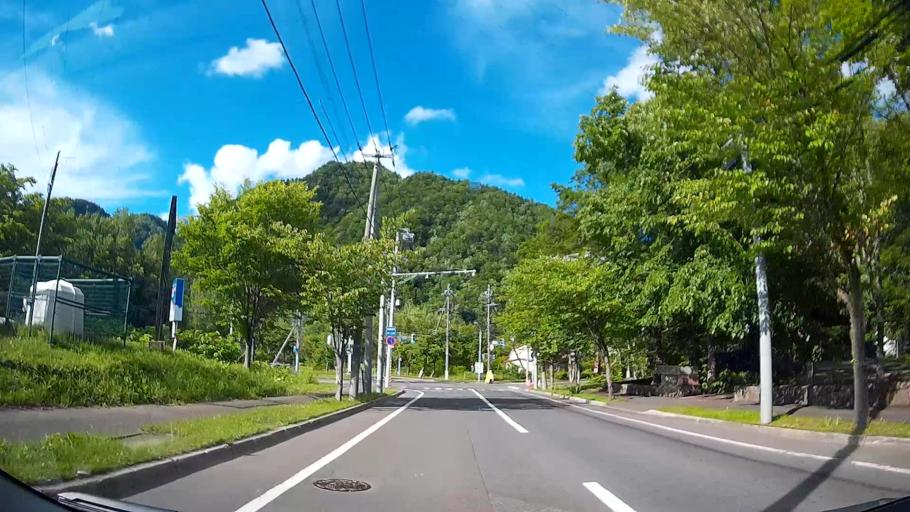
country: JP
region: Hokkaido
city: Sapporo
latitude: 42.9724
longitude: 141.1655
